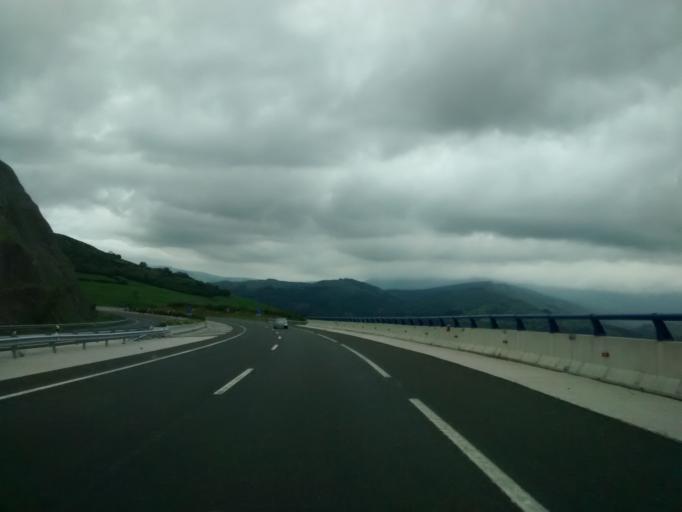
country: ES
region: Cantabria
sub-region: Provincia de Cantabria
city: Barcena de Pie de Concha
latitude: 43.1317
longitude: -4.0693
